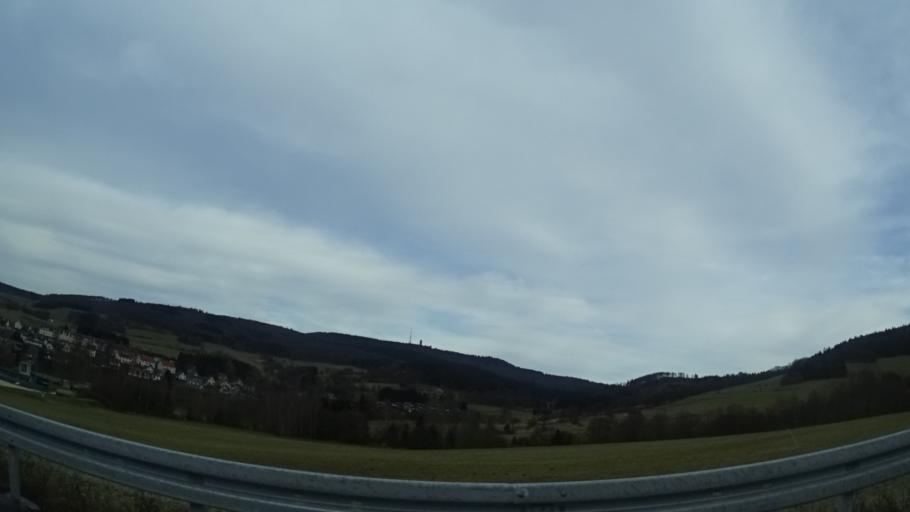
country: DE
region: Thuringia
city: Brotterode
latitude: 50.8219
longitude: 10.4554
